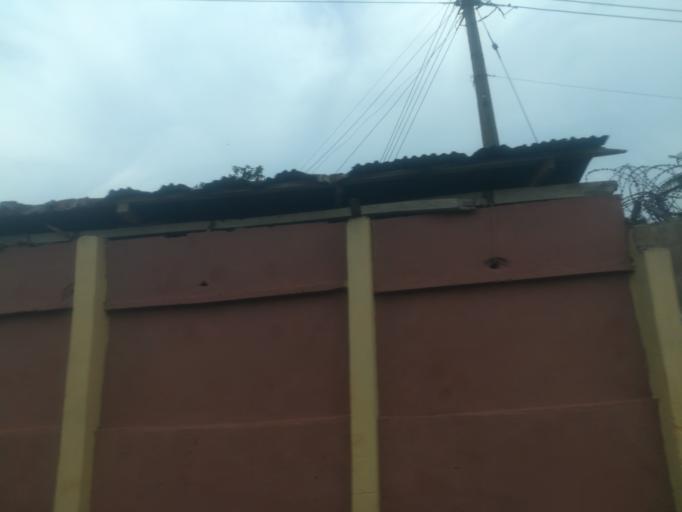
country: NG
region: Oyo
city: Ibadan
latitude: 7.4166
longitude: 3.9014
